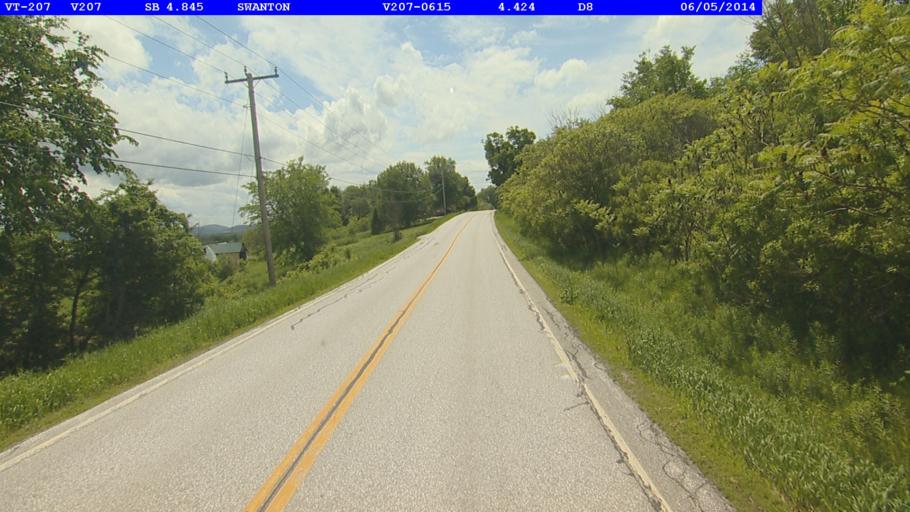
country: US
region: Vermont
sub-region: Franklin County
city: Swanton
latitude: 44.9072
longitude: -73.0625
